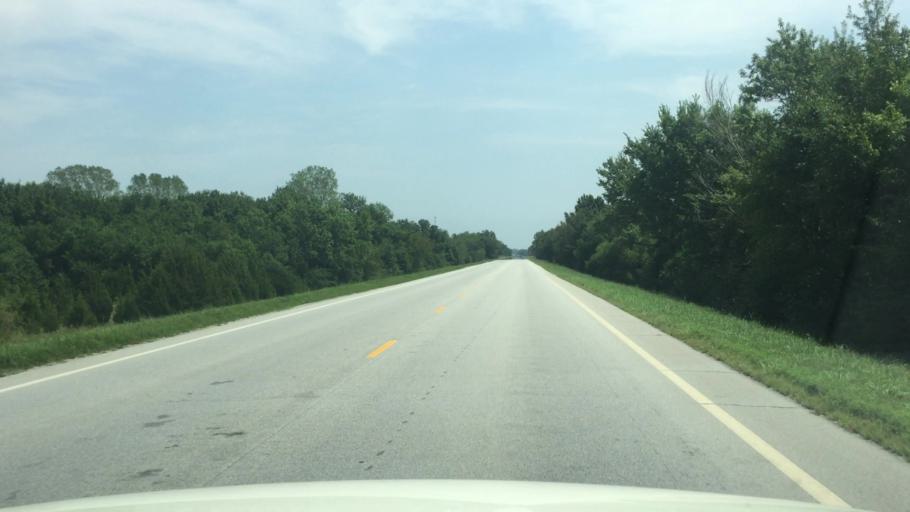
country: US
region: Kansas
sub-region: Cherokee County
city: Columbus
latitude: 37.1788
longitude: -94.8763
